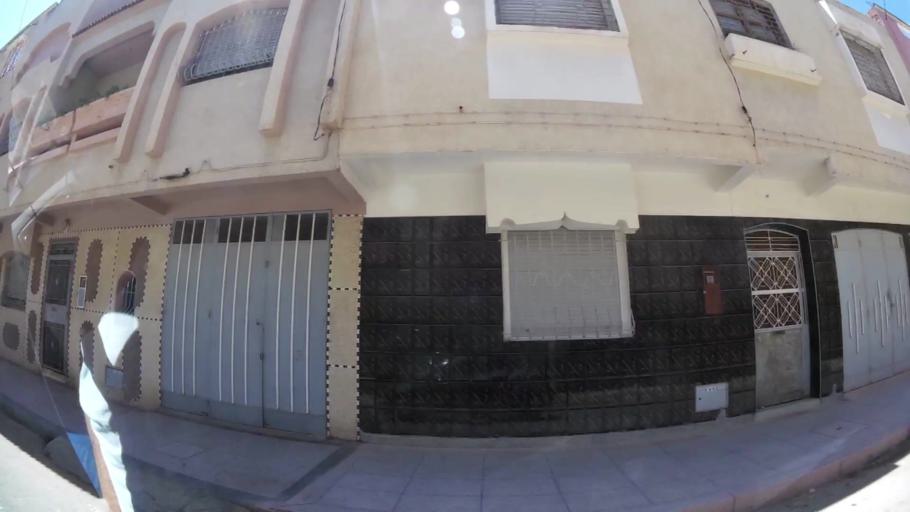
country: MA
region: Oriental
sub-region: Oujda-Angad
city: Oujda
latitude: 34.6796
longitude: -1.9407
